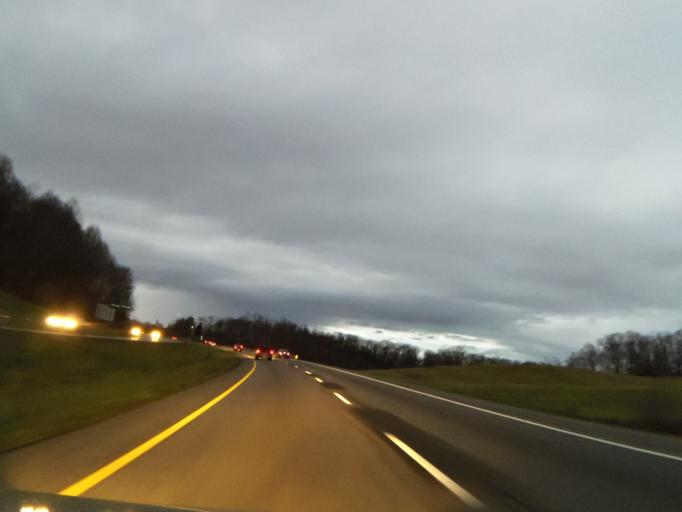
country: US
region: Tennessee
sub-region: Washington County
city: Oak Grove
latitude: 36.3947
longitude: -82.4499
